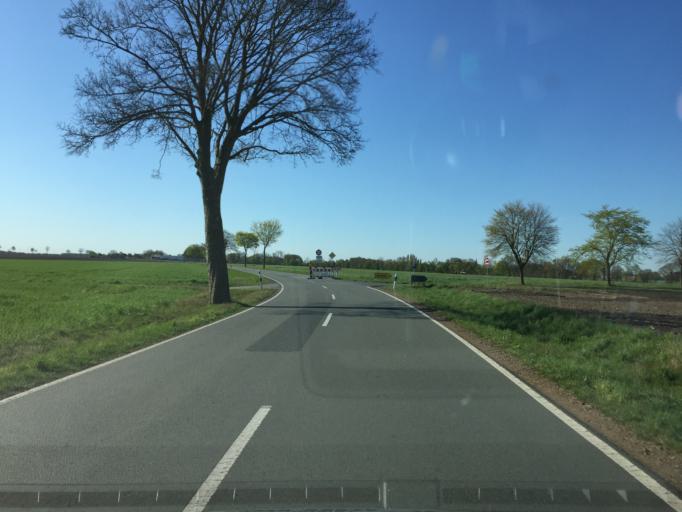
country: DE
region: Lower Saxony
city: Varrel
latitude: 52.6333
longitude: 8.7377
